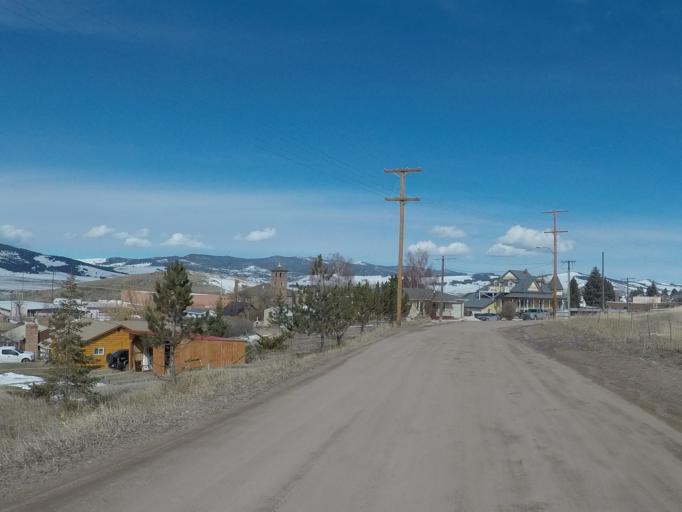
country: US
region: Montana
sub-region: Granite County
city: Philipsburg
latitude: 46.3274
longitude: -113.2927
